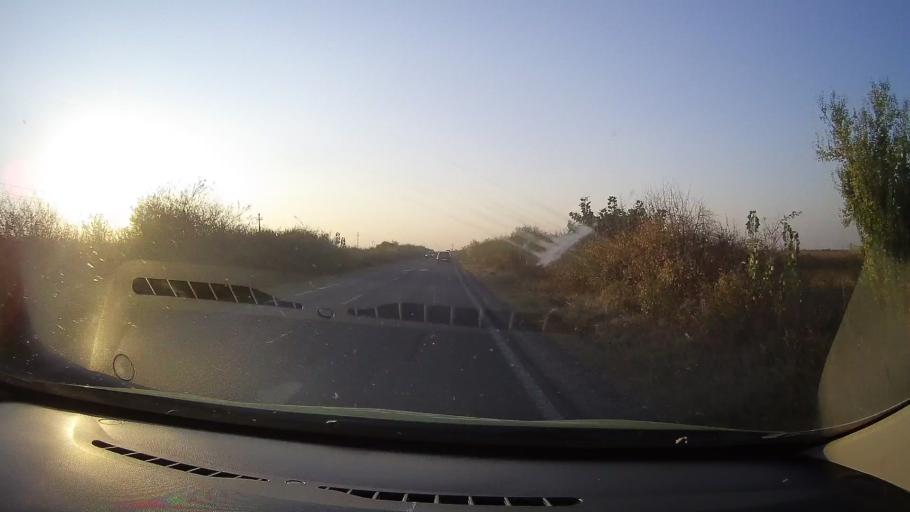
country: RO
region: Arad
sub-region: Comuna Bocsig
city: Bocsig
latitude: 46.4202
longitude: 21.9601
